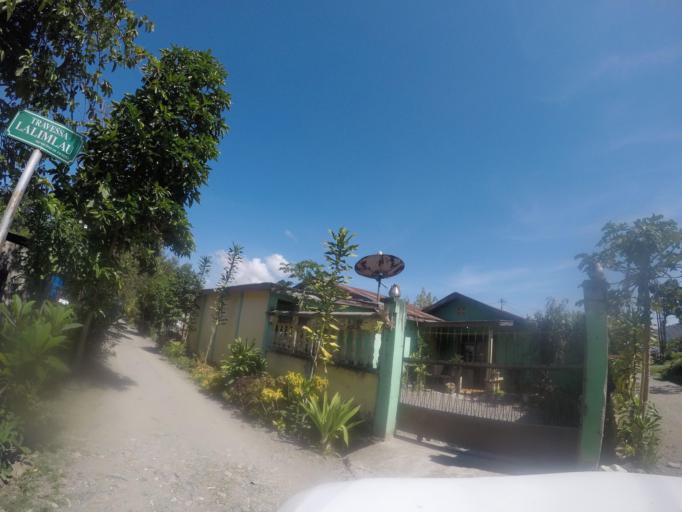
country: TL
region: Ermera
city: Gleno
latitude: -8.7286
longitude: 125.4307
